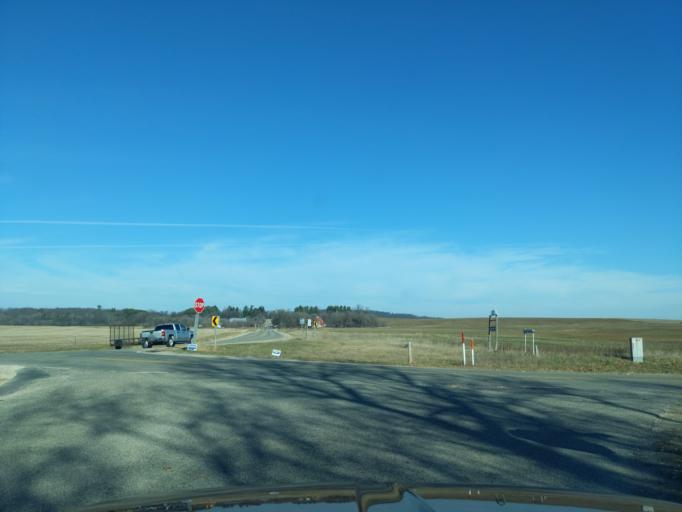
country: US
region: Wisconsin
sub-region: Waushara County
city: Silver Lake
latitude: 44.0927
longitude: -89.1889
